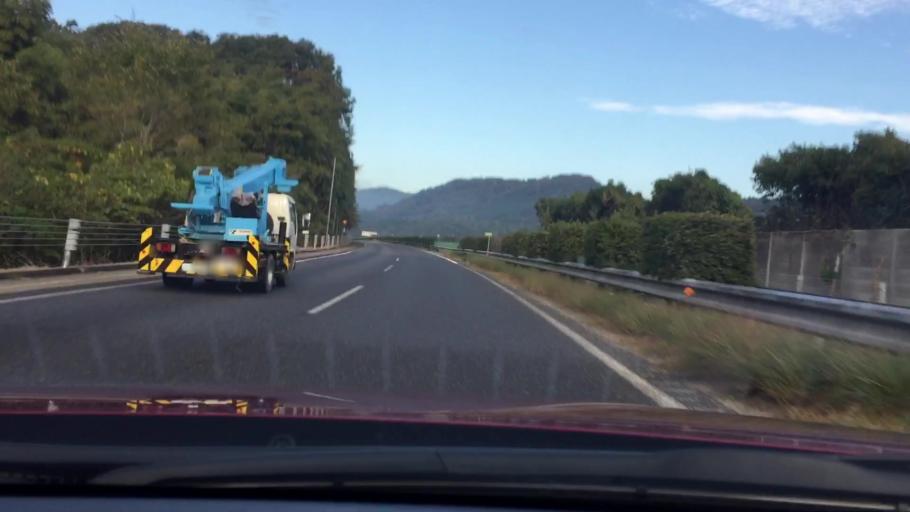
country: JP
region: Hyogo
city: Yamazakicho-nakabirose
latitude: 34.9677
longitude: 134.6749
